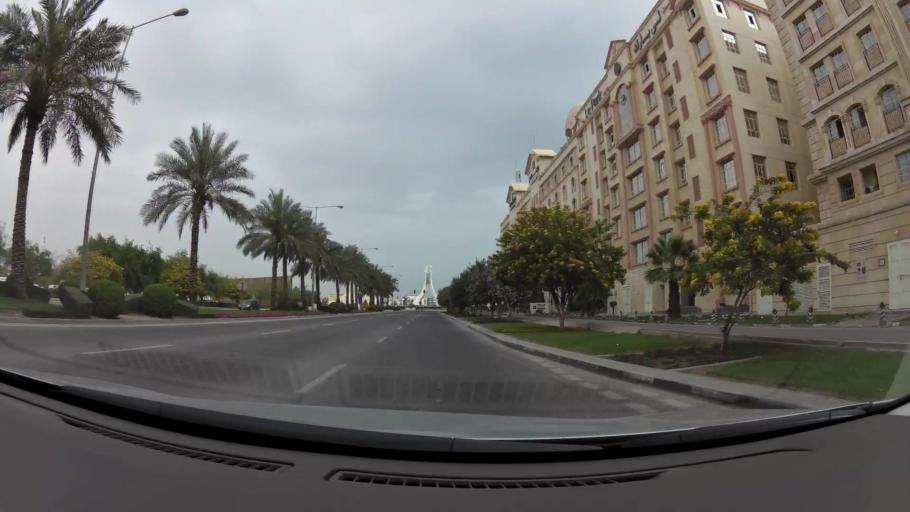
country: QA
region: Baladiyat ad Dawhah
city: Doha
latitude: 25.2905
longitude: 51.4964
